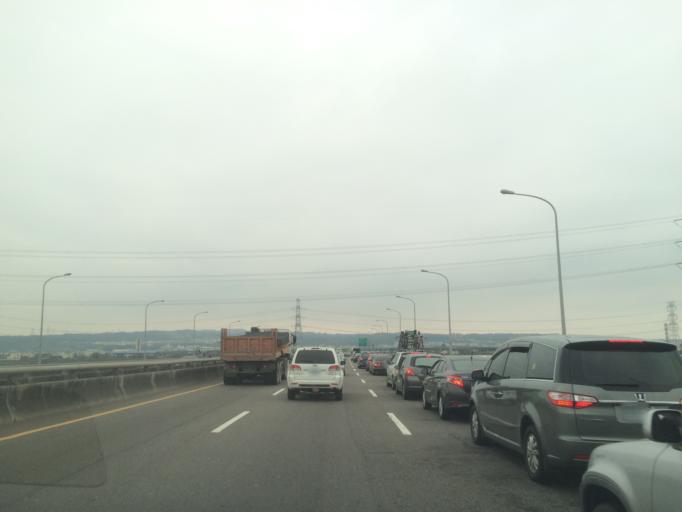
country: TW
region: Taiwan
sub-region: Changhua
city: Chang-hua
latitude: 24.0992
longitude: 120.6104
